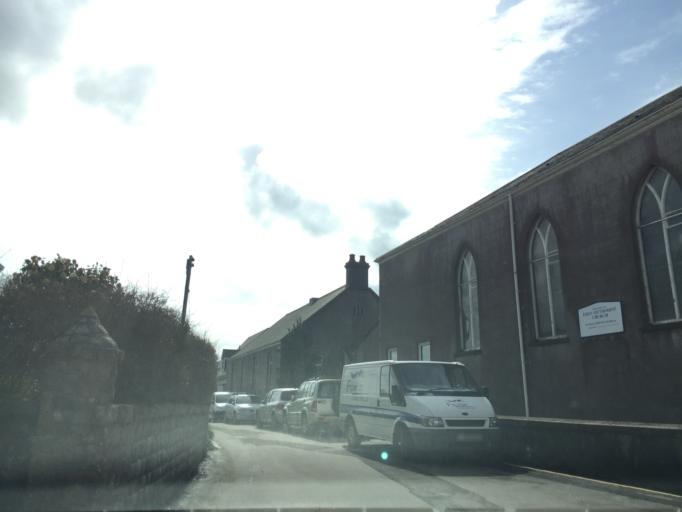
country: JE
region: St Helier
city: Saint Helier
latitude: 49.2042
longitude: -2.0713
